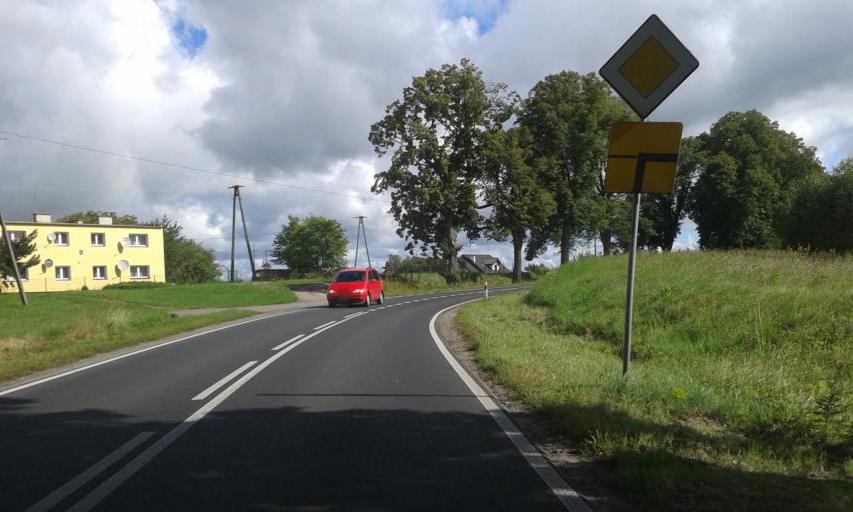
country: PL
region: West Pomeranian Voivodeship
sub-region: Powiat koszalinski
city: Bobolice
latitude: 53.9597
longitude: 16.5983
